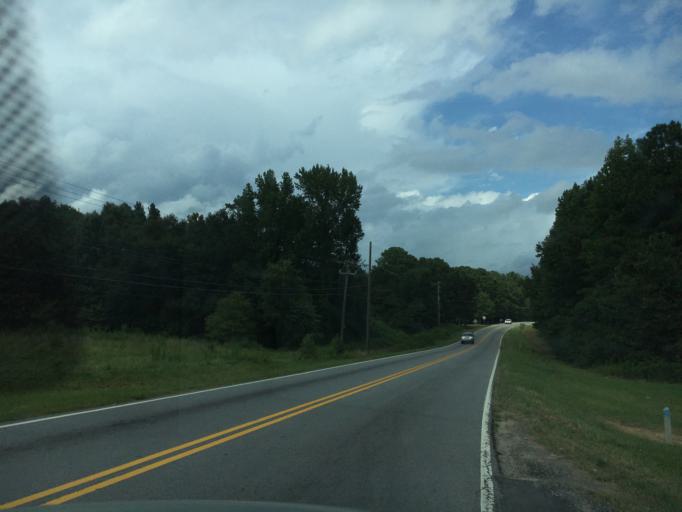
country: US
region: Georgia
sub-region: Rockdale County
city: Lakeview Estates
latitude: 33.7560
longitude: -84.0174
